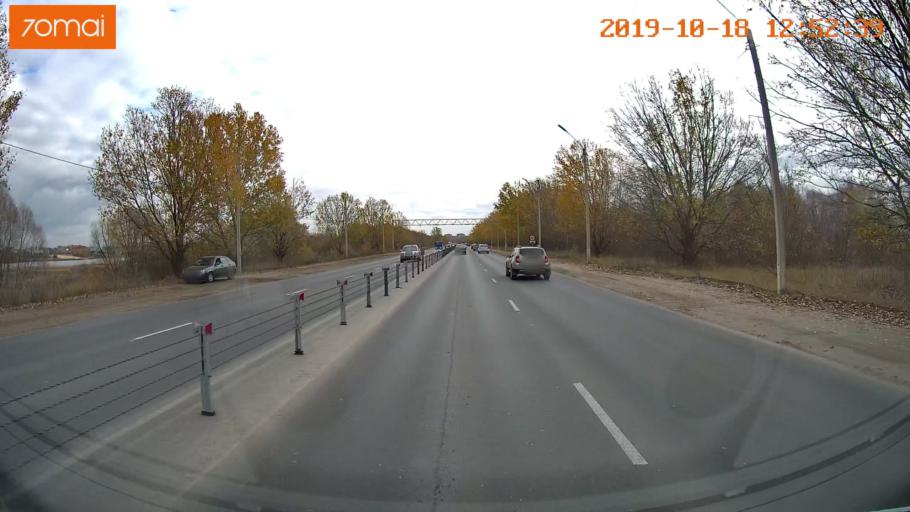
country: RU
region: Rjazan
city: Ryazan'
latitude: 54.6506
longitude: 39.6964
